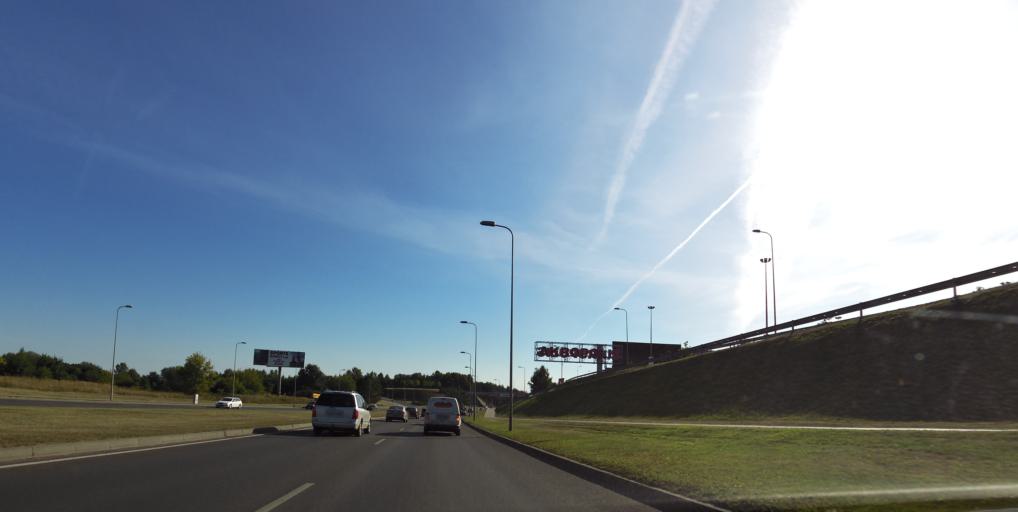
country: LT
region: Vilnius County
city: Seskine
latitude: 54.7118
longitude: 25.2598
